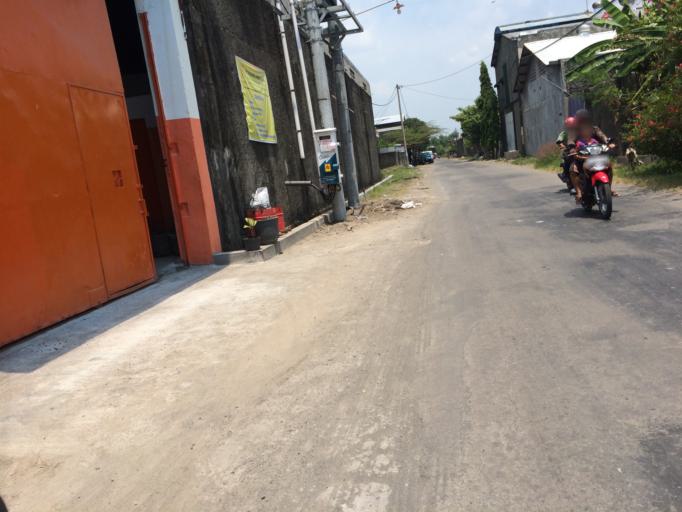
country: ID
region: Central Java
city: Grogol
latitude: -7.6166
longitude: 110.8269
